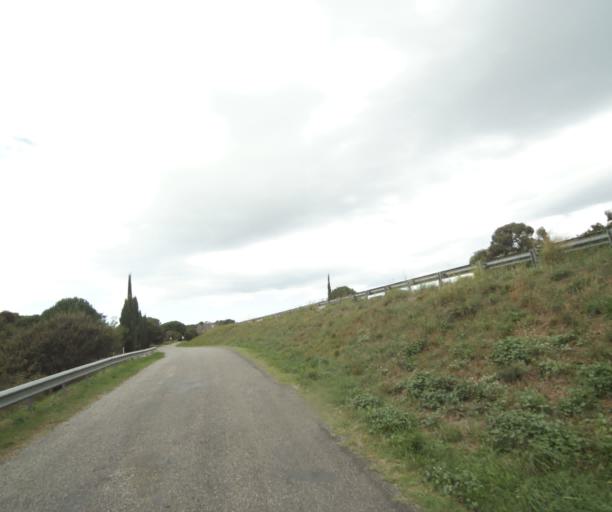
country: FR
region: Languedoc-Roussillon
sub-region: Departement des Pyrenees-Orientales
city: Argelers
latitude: 42.5418
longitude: 3.0145
